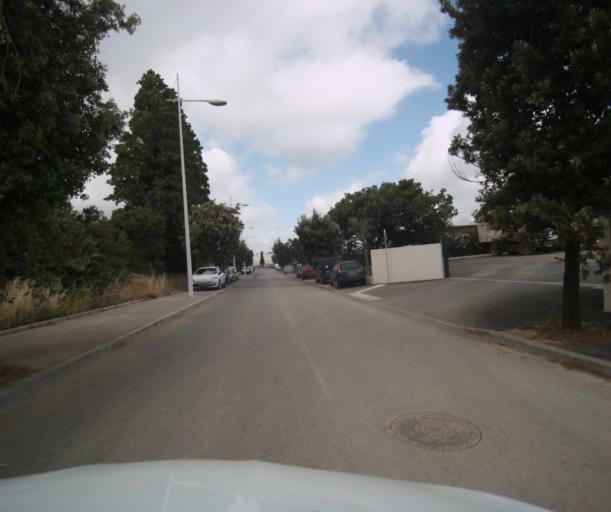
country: FR
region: Provence-Alpes-Cote d'Azur
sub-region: Departement du Var
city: Six-Fours-les-Plages
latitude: 43.1138
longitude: 5.8458
